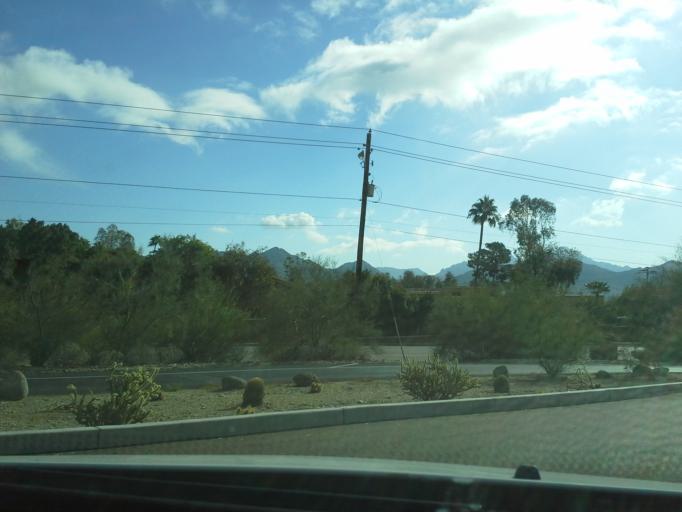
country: US
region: Arizona
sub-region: Maricopa County
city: Glendale
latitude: 33.5812
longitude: -112.0657
